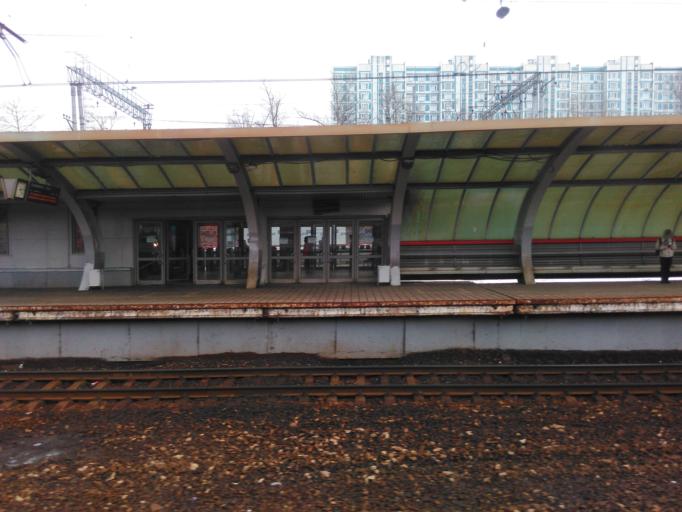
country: RU
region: Moscow
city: Yaroslavskiy
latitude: 55.8801
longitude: 37.7105
